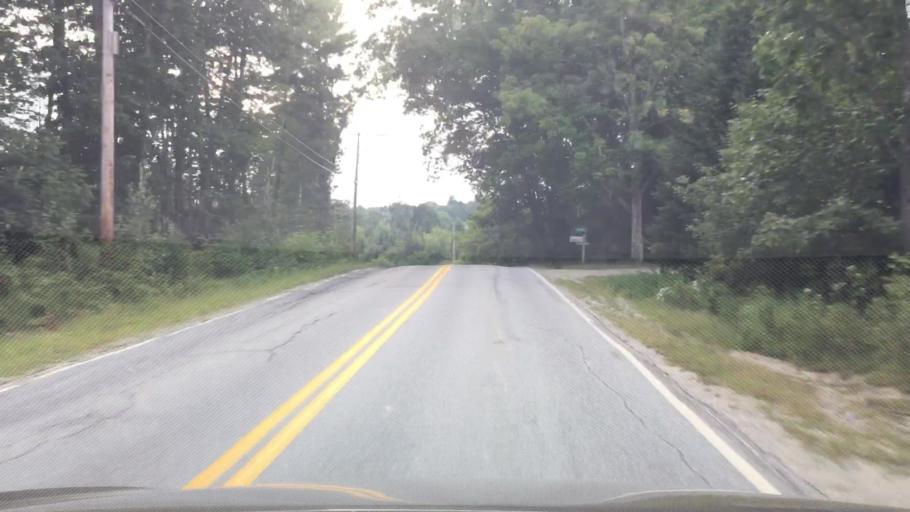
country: US
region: Maine
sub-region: Hancock County
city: Penobscot
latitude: 44.4723
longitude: -68.7314
